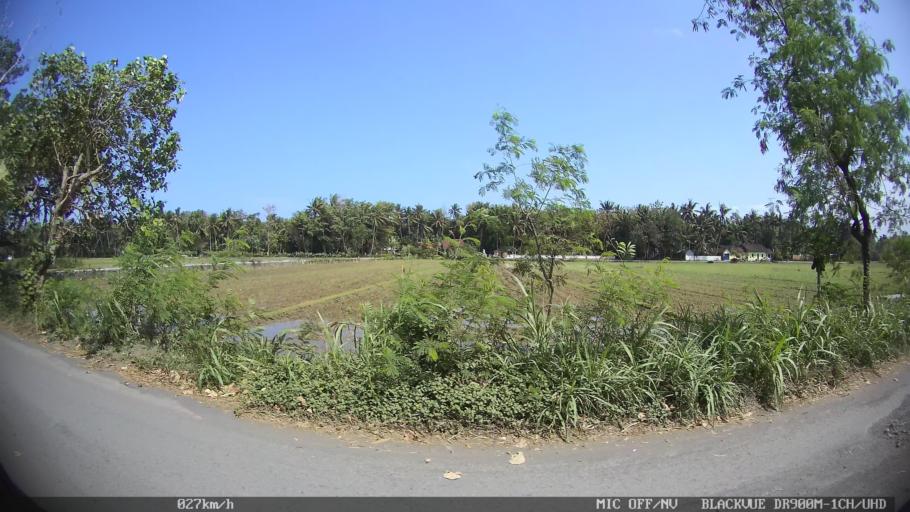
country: ID
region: Daerah Istimewa Yogyakarta
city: Srandakan
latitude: -7.9582
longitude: 110.2161
